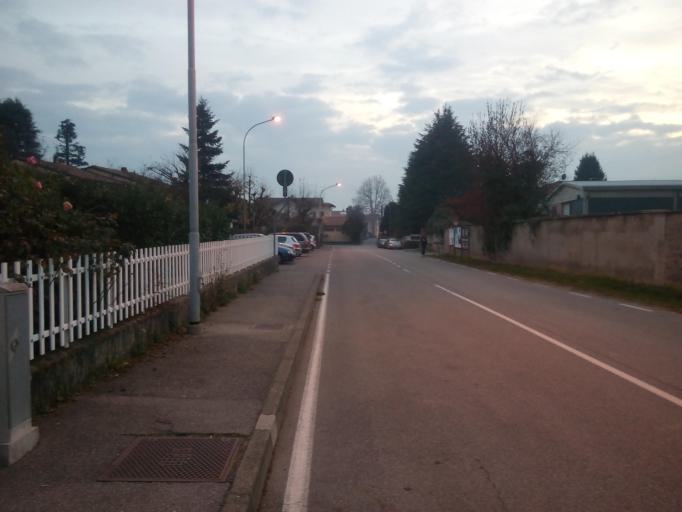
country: IT
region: Lombardy
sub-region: Provincia di Lecco
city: Verderio Superiore
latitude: 45.6698
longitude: 9.4425
